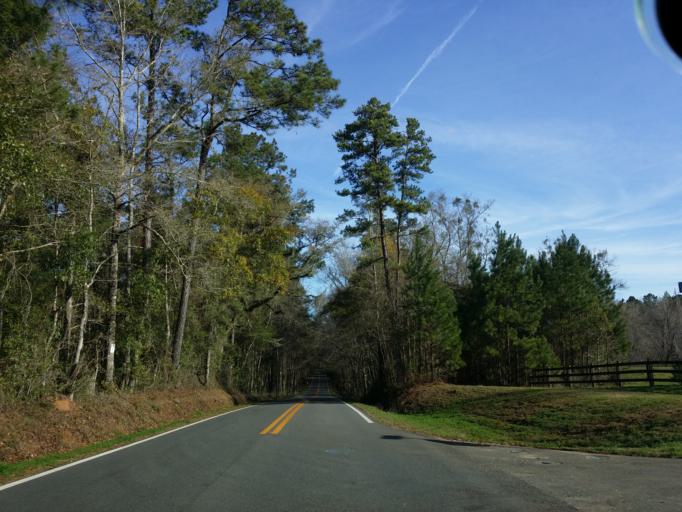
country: US
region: Florida
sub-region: Leon County
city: Woodville
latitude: 30.3849
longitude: -84.1553
